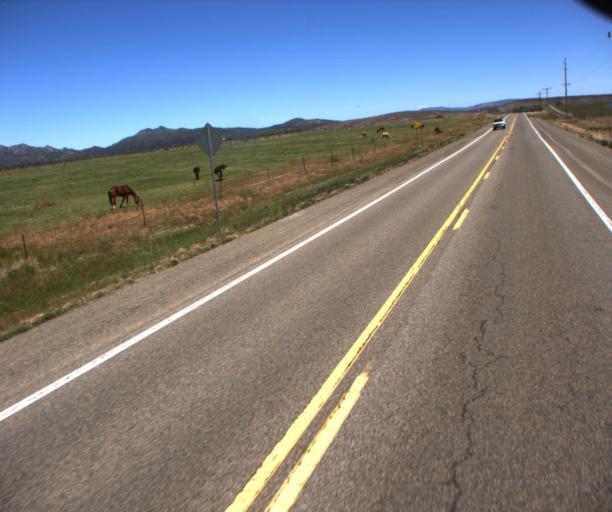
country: US
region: Arizona
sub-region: Yavapai County
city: Congress
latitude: 34.2826
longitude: -112.7227
